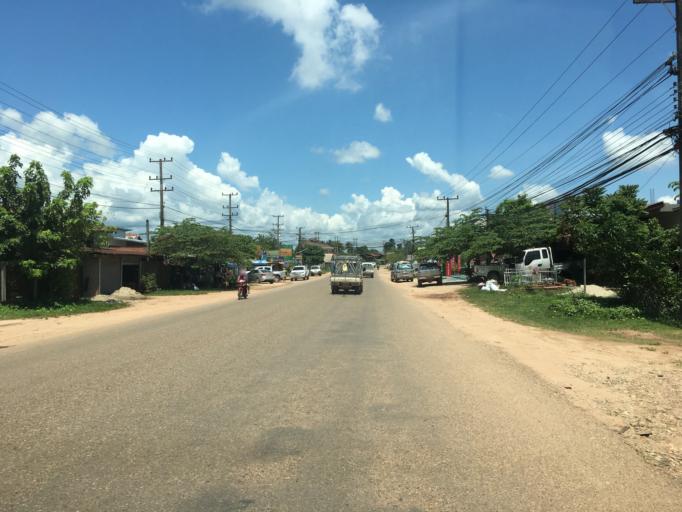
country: LA
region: Vientiane
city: Vientiane
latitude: 18.0664
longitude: 102.5365
